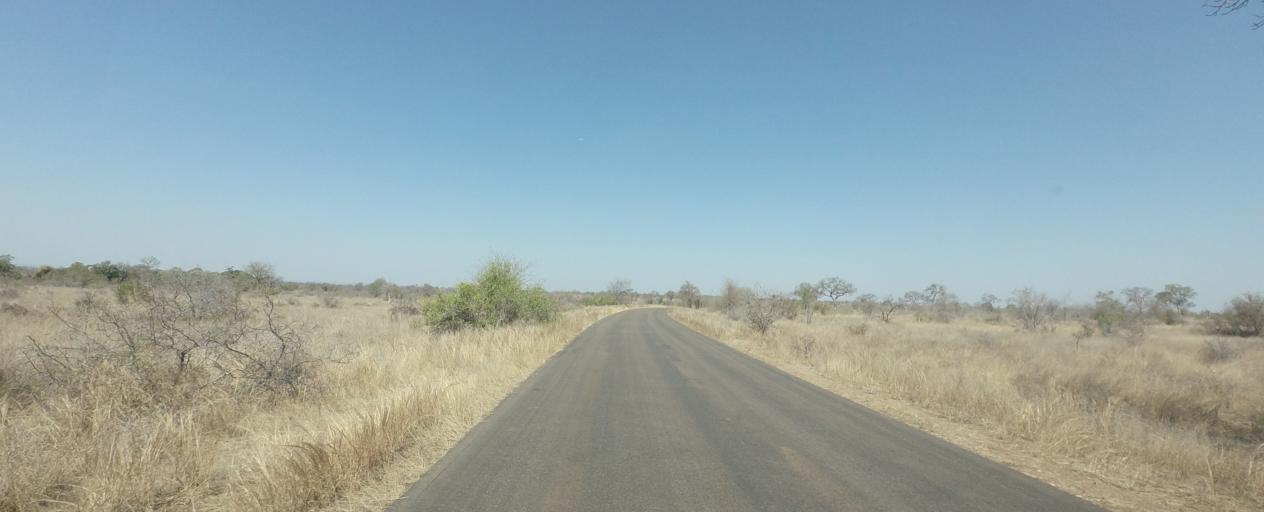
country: ZA
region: Limpopo
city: Thulamahashi
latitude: -24.4030
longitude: 31.7772
